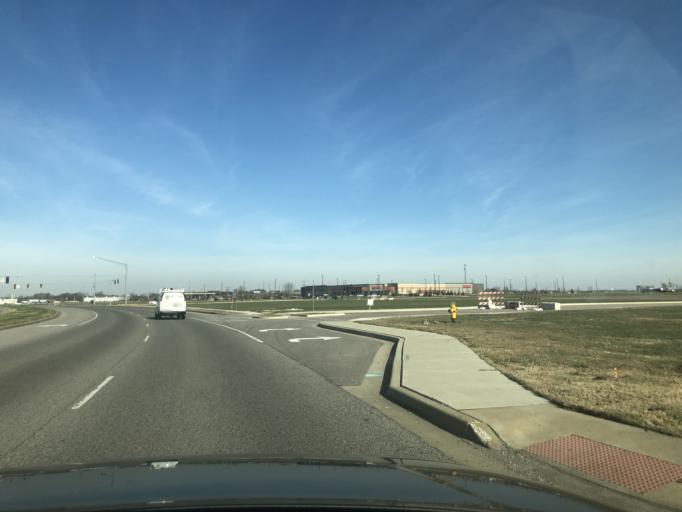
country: US
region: Indiana
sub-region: Vanderburgh County
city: Melody Hill
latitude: 37.9837
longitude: -87.4625
